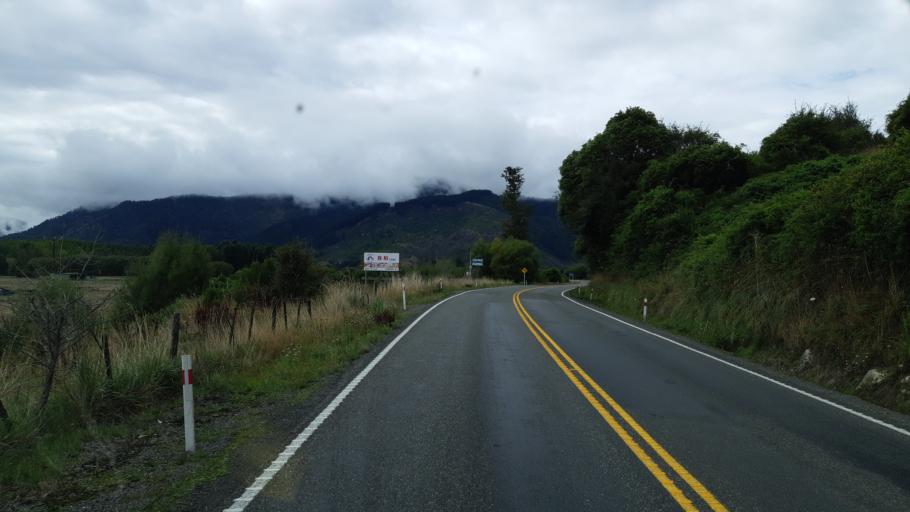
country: NZ
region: West Coast
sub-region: Buller District
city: Westport
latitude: -41.7974
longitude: 172.3112
